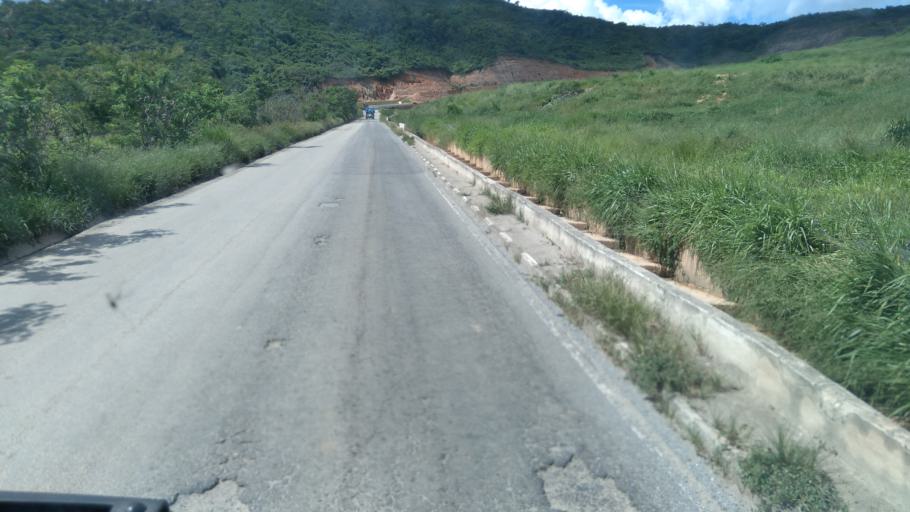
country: BR
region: Minas Gerais
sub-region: Santa Luzia
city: Santa Luzia
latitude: -19.8552
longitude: -43.8497
